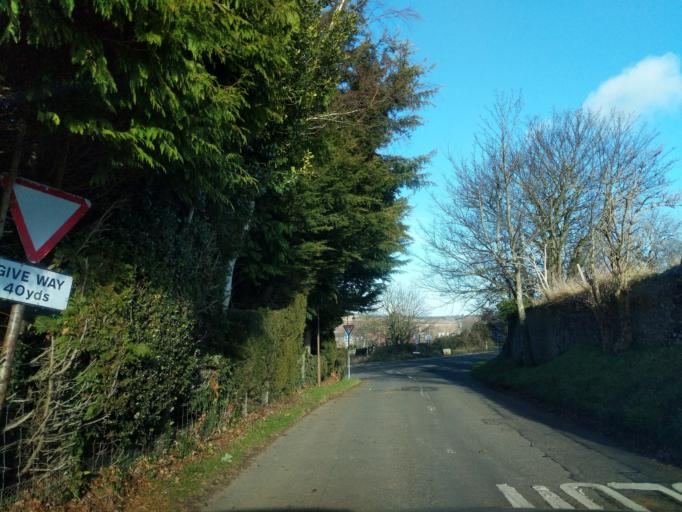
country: GB
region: Scotland
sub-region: East Lothian
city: East Linton
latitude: 55.9832
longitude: -2.6545
